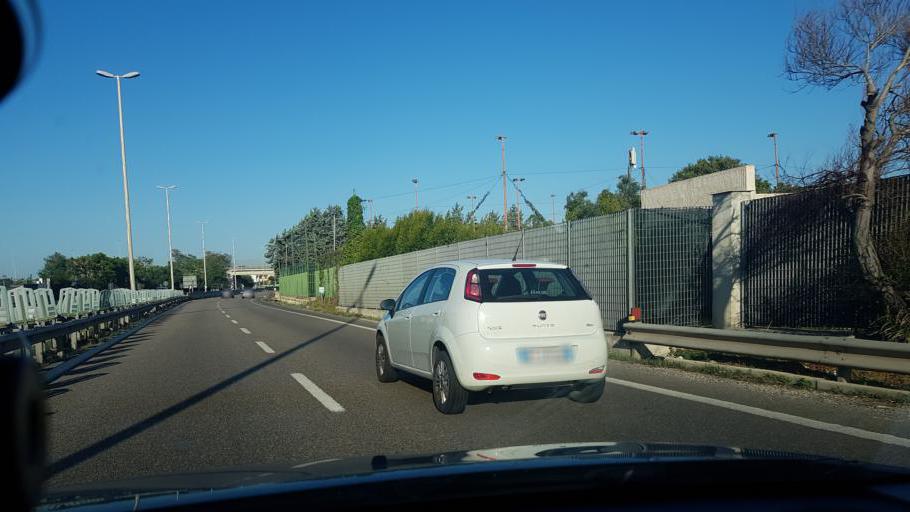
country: IT
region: Apulia
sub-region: Provincia di Bari
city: Parco Scizzo-Parchitello
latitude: 41.0840
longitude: 16.9957
